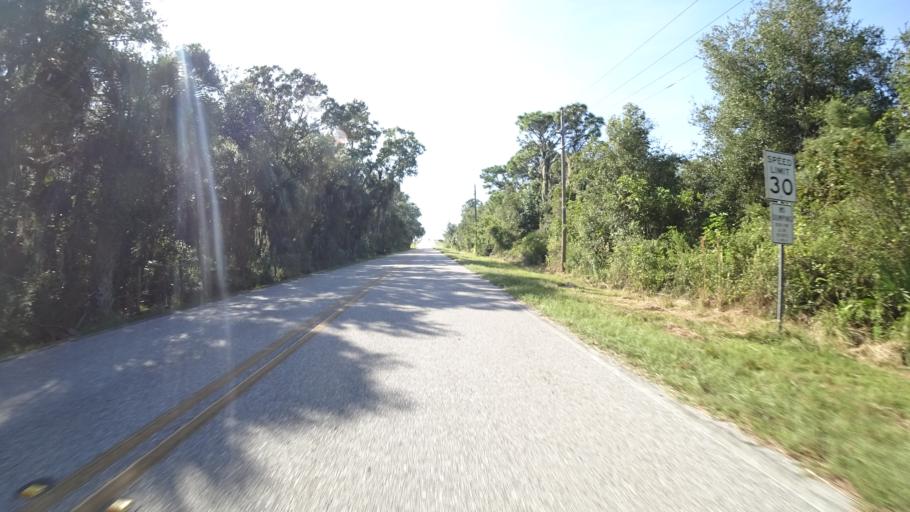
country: US
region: Florida
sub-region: Sarasota County
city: The Meadows
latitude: 27.4178
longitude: -82.4517
